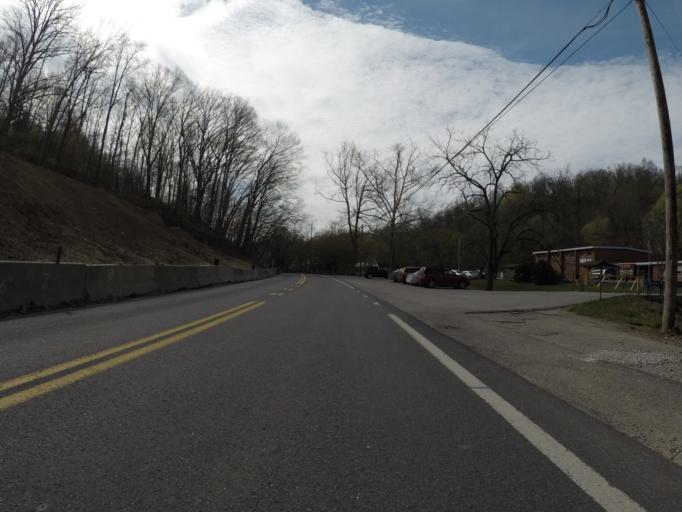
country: US
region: West Virginia
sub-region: Cabell County
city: Pea Ridge
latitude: 38.3828
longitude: -82.3766
